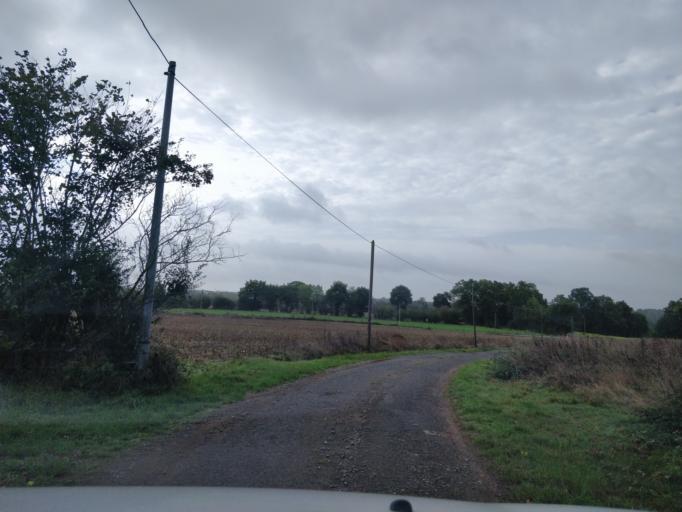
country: FR
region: Brittany
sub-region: Departement d'Ille-et-Vilaine
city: Liffre
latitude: 48.2139
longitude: -1.4789
